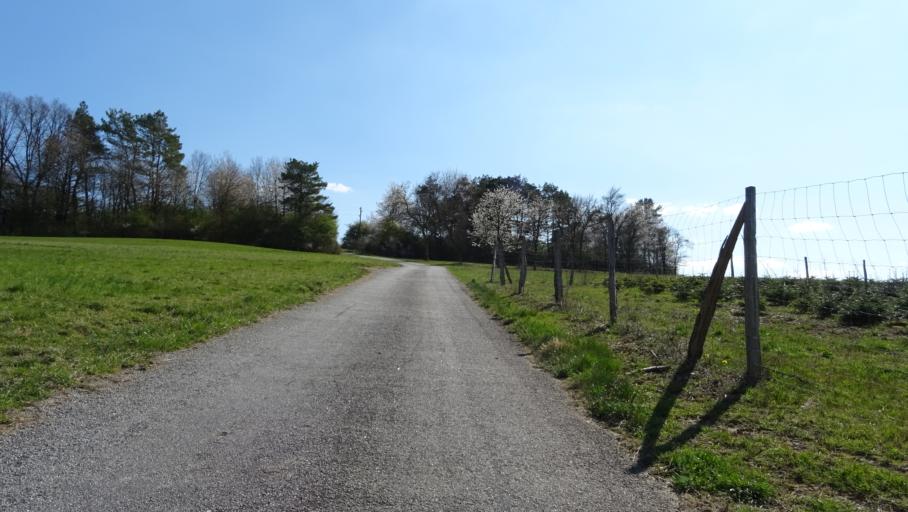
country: DE
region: Baden-Wuerttemberg
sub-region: Karlsruhe Region
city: Billigheim
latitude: 49.3985
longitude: 9.2313
